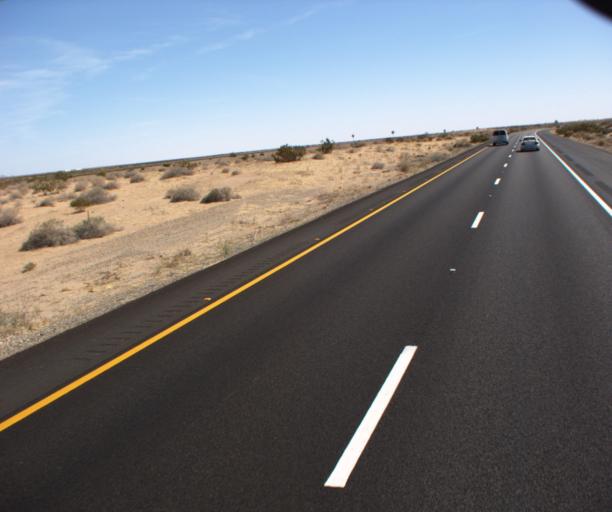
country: US
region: Arizona
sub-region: Yuma County
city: Fortuna Foothills
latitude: 32.6250
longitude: -114.5212
